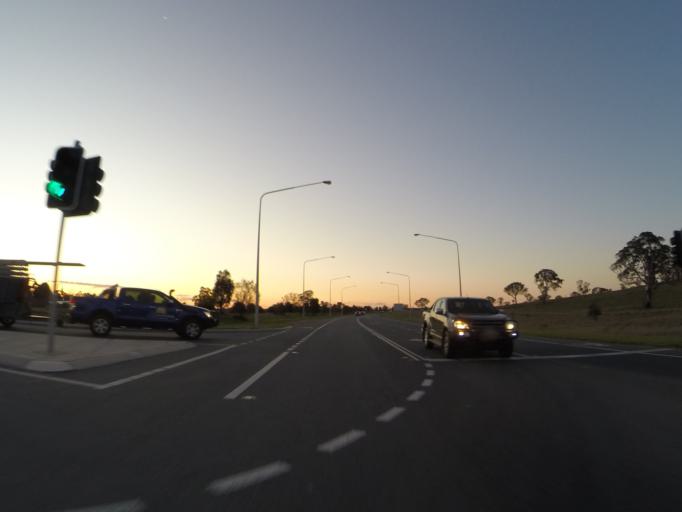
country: AU
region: Australian Capital Territory
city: Kaleen
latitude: -35.2003
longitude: 149.1654
